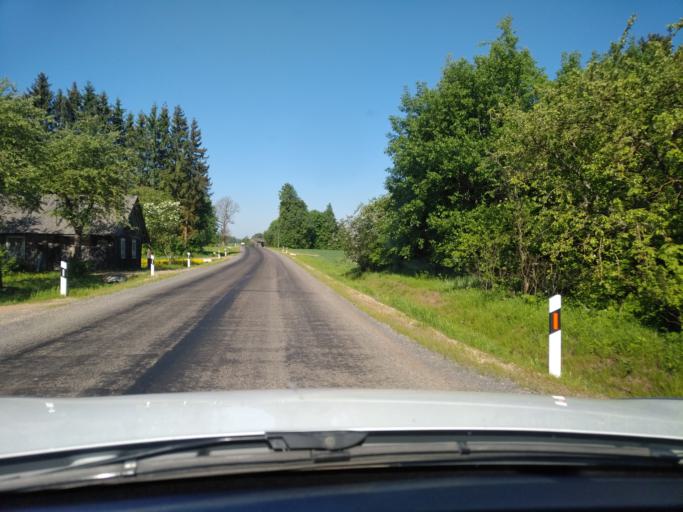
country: LT
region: Panevezys
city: Rokiskis
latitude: 55.7320
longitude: 25.5238
